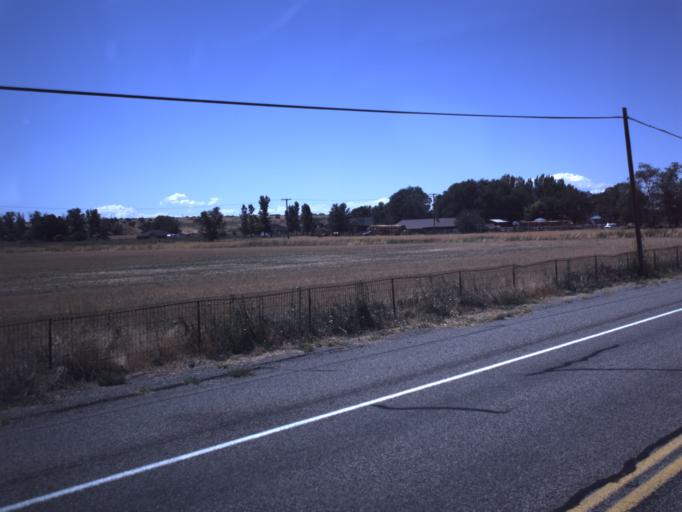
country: US
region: Utah
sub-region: Millard County
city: Delta
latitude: 39.5340
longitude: -112.2930
